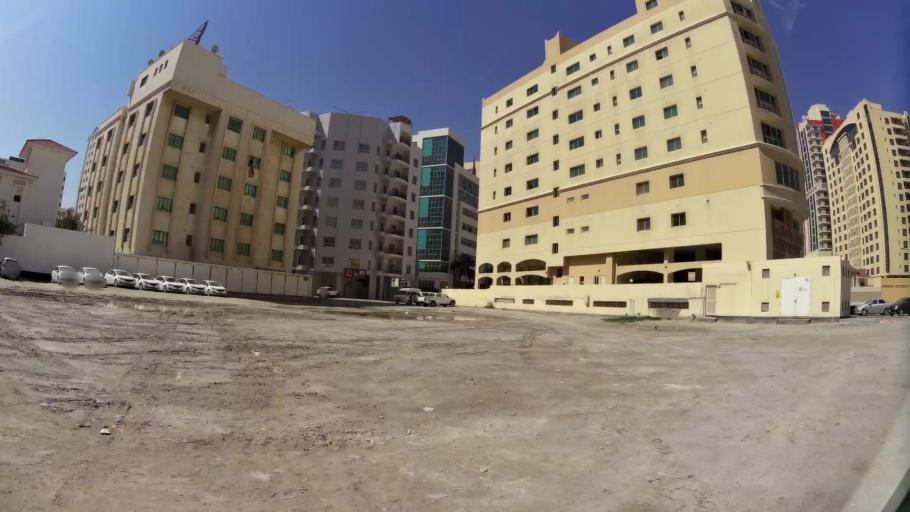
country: BH
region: Manama
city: Manama
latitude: 26.2150
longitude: 50.6052
